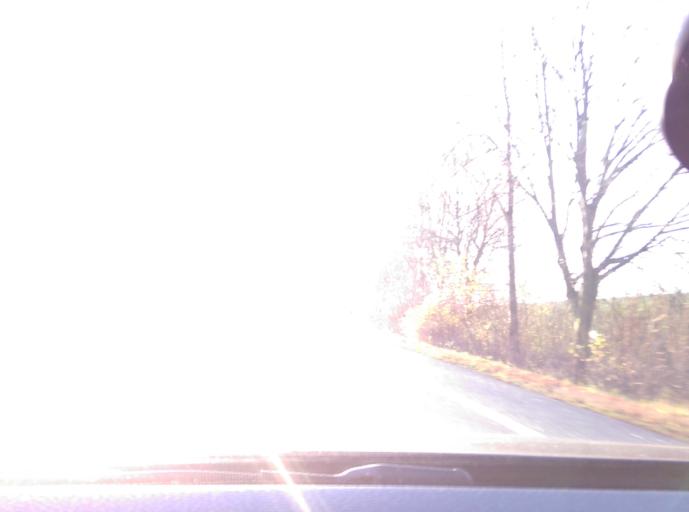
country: DE
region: Lower Saxony
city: Gemeinde Friedland
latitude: 51.3988
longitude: 9.9059
